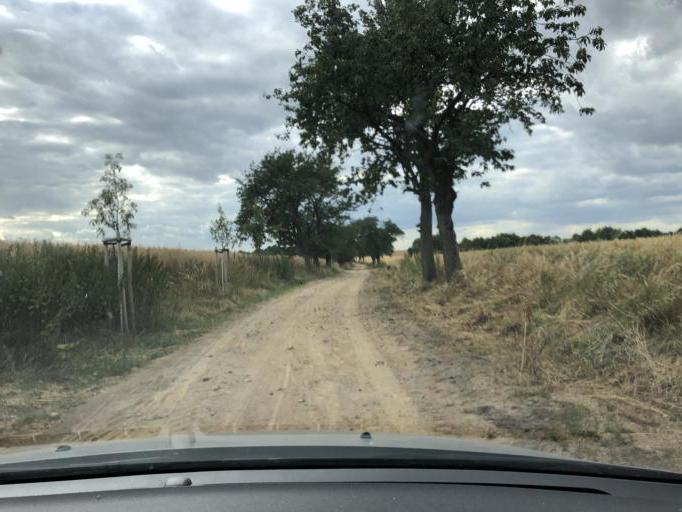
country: DE
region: Saxony
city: Geithain
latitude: 51.0257
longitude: 12.6383
